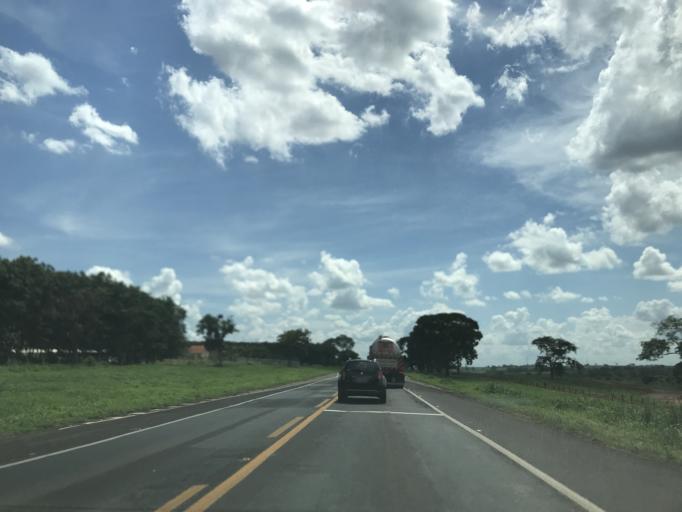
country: BR
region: Sao Paulo
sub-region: Nova Granada
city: Nova Granada
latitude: -20.4109
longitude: -49.2537
